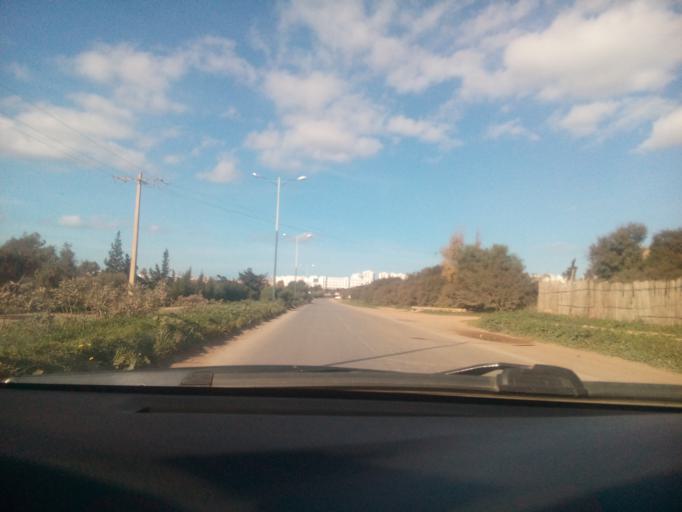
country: DZ
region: Oran
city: Bir el Djir
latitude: 35.6867
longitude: -0.5738
